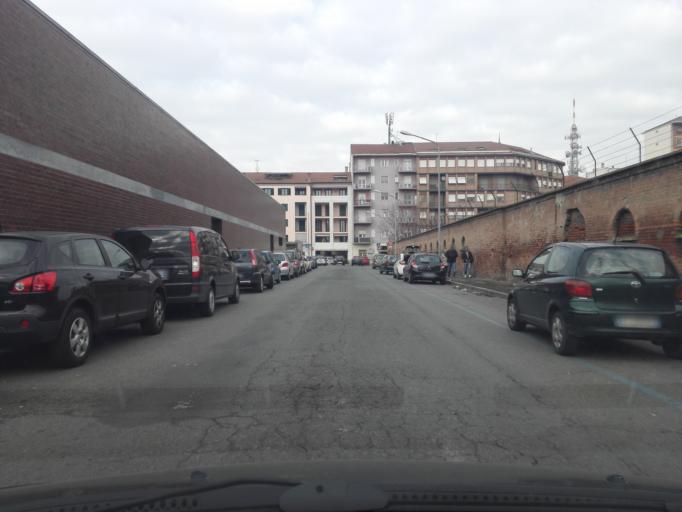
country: IT
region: Piedmont
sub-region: Provincia di Alessandria
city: Alessandria
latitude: 44.9082
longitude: 8.6178
